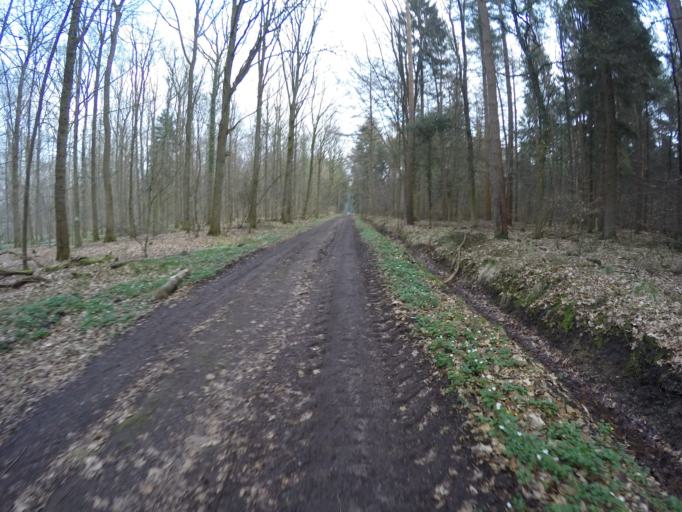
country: DE
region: Schleswig-Holstein
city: Borstel-Hohenraden
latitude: 53.7224
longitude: 9.8094
